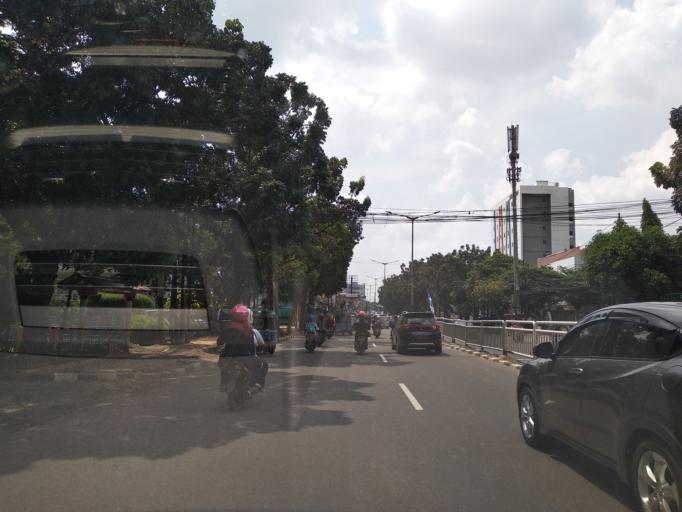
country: ID
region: Jakarta Raya
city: Jakarta
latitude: -6.2362
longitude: 106.8444
